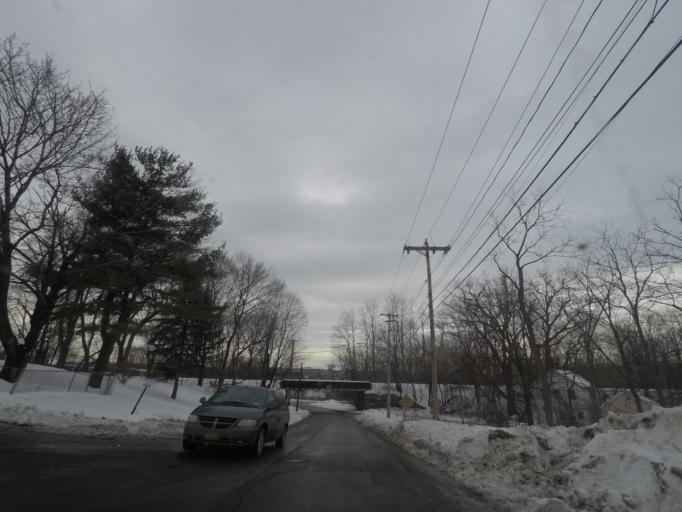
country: US
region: New York
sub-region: Rensselaer County
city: Rensselaer
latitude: 42.6340
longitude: -73.7413
